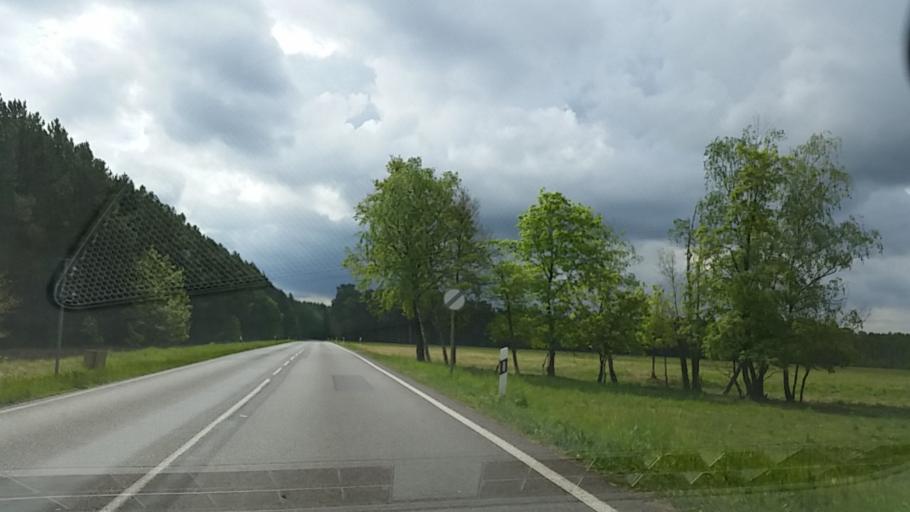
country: DE
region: Brandenburg
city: Spreenhagen
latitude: 52.3099
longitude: 13.9007
